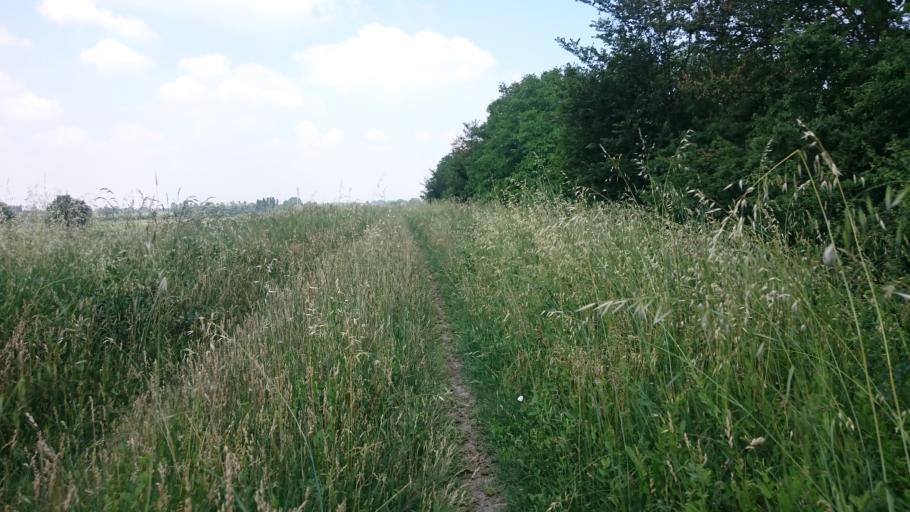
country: IT
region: Lombardy
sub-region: Provincia di Mantova
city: San Biagio
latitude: 45.1147
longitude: 10.8566
